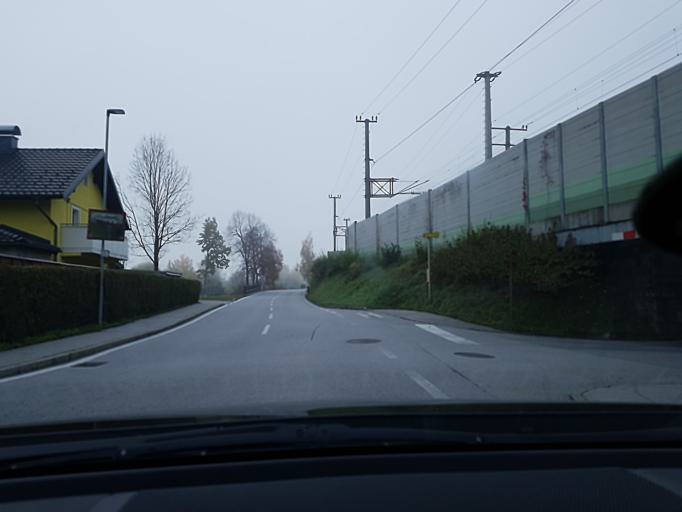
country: AT
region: Salzburg
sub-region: Politischer Bezirk Sankt Johann im Pongau
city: Sankt Johann im Pongau
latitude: 47.3446
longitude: 13.1948
